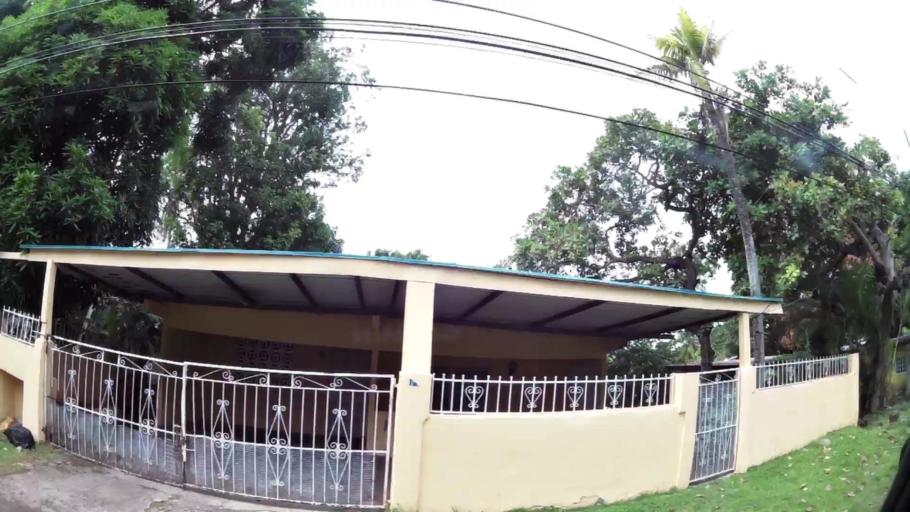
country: PA
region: Panama
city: San Miguelito
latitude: 9.0426
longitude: -79.4325
